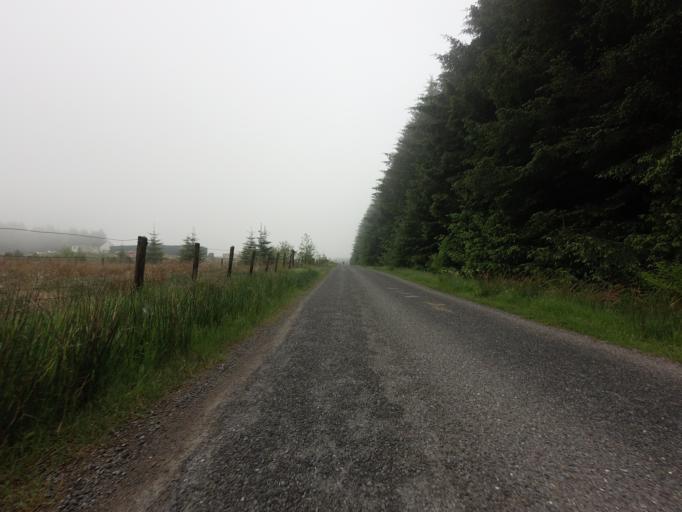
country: GB
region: Scotland
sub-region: Perth and Kinross
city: Kinross
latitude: 56.1499
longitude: -3.4532
